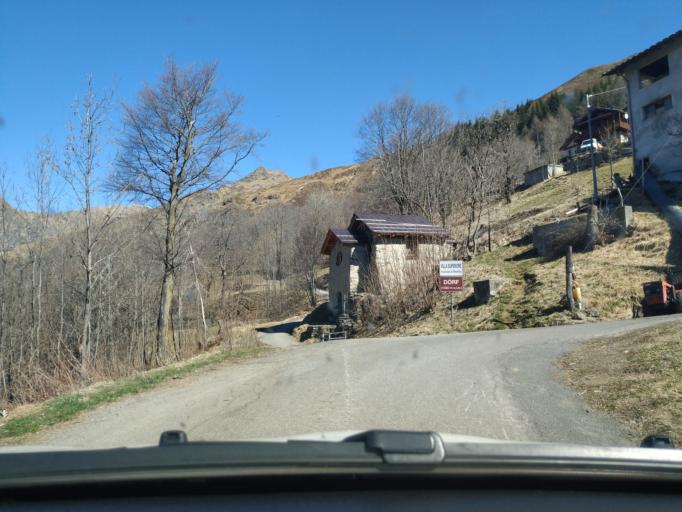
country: IT
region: Piedmont
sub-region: Provincia di Vercelli
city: Rimella
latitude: 45.9092
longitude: 8.1862
